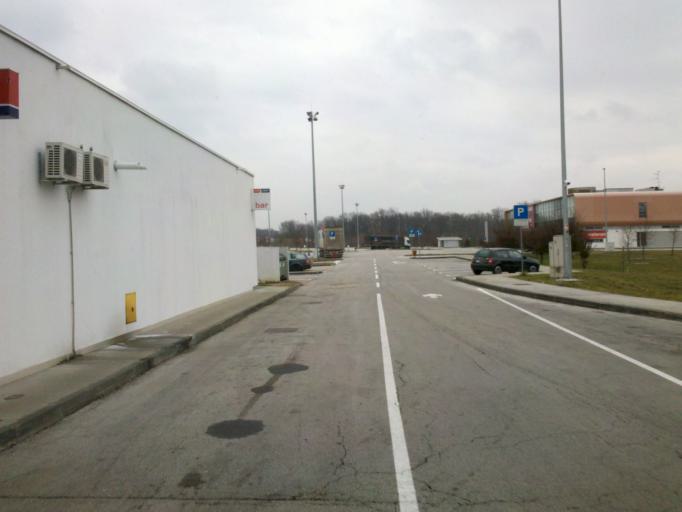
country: HR
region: Zagrebacka
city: Jastrebarsko
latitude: 45.6609
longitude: 15.7104
